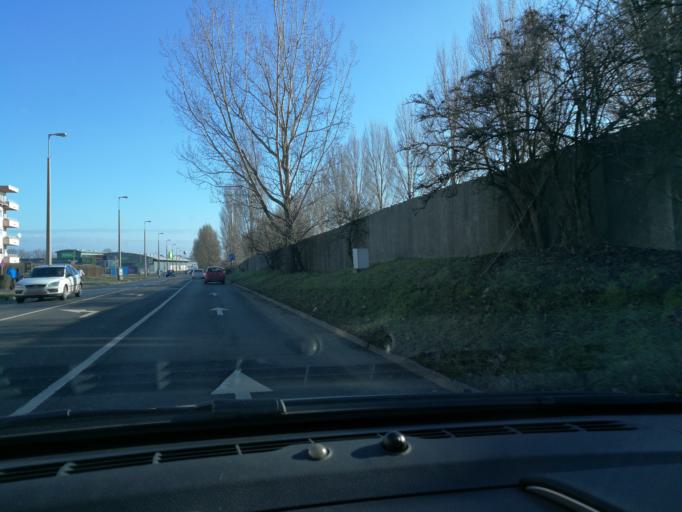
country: HU
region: Szabolcs-Szatmar-Bereg
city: Nyiregyhaza
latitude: 47.9720
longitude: 21.7308
